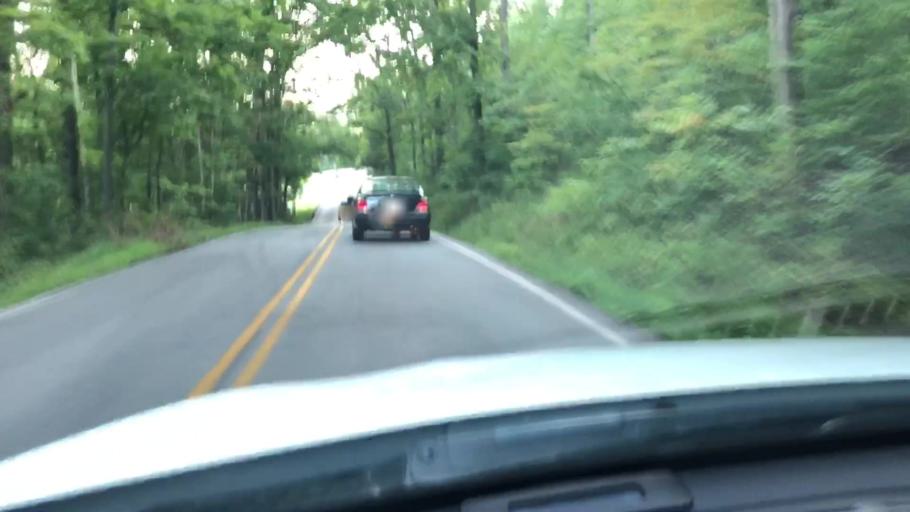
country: US
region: Kentucky
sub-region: Jefferson County
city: Middletown
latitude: 38.1977
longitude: -85.4899
